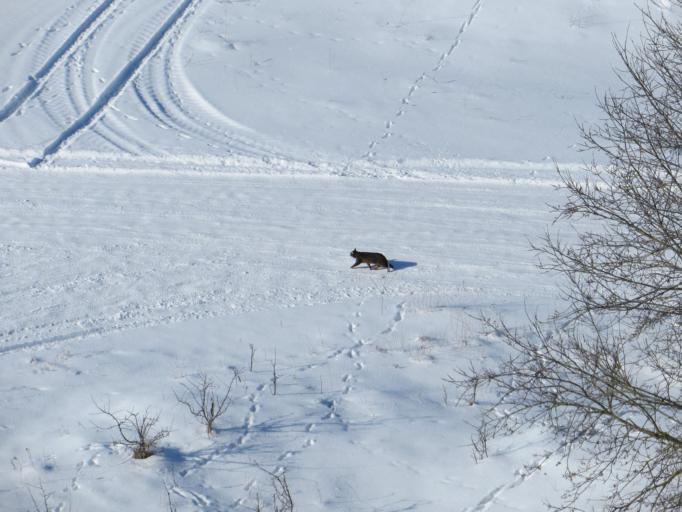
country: LT
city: Zarasai
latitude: 55.7730
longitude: 25.9950
